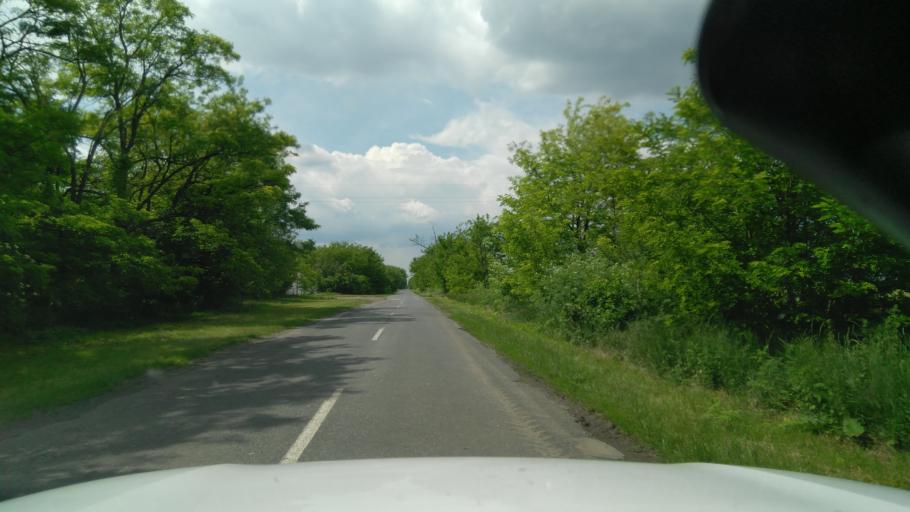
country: HU
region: Bekes
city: Magyarbanhegyes
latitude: 46.4654
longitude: 20.9508
